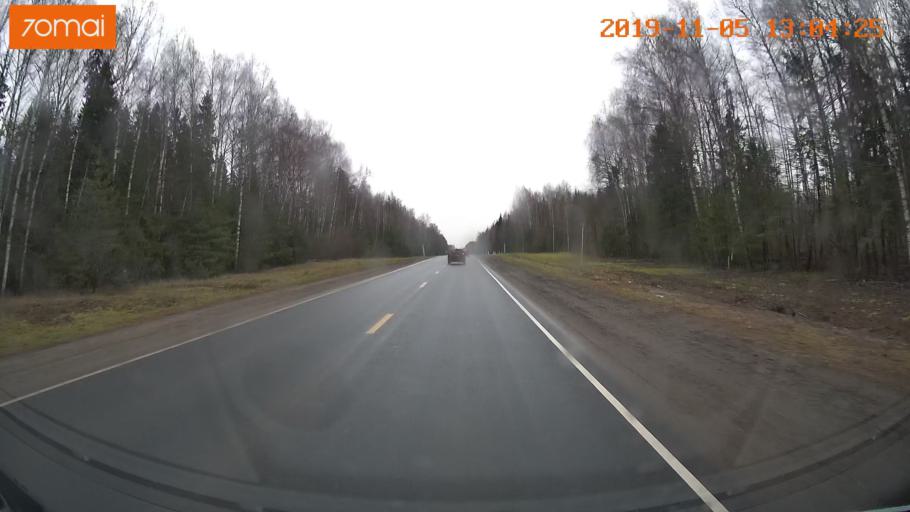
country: RU
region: Ivanovo
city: Kitovo
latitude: 56.8892
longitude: 41.2208
